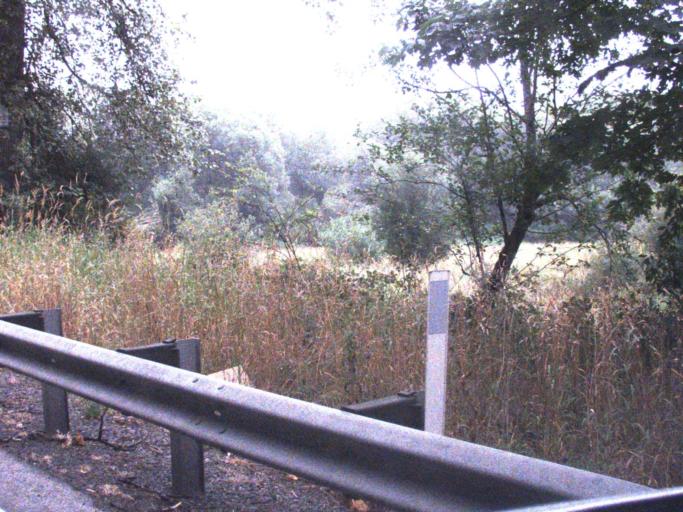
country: US
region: Washington
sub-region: King County
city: Lake Marcel-Stillwater
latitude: 47.6914
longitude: -121.9550
